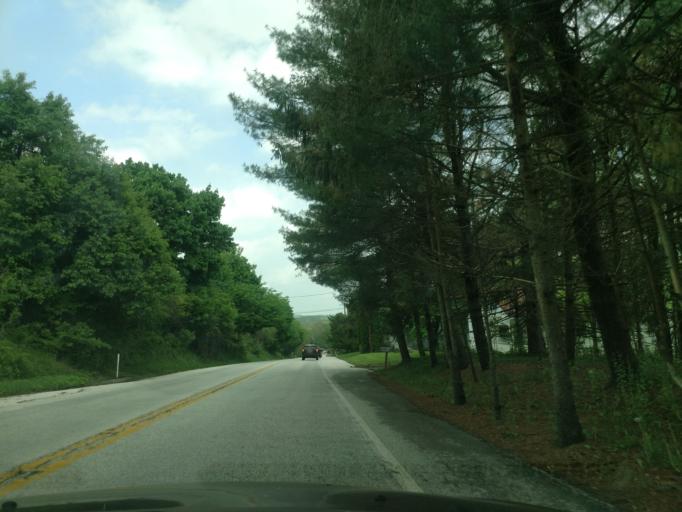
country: US
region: Pennsylvania
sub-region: Montgomery County
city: Stowe
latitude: 40.1702
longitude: -75.7337
